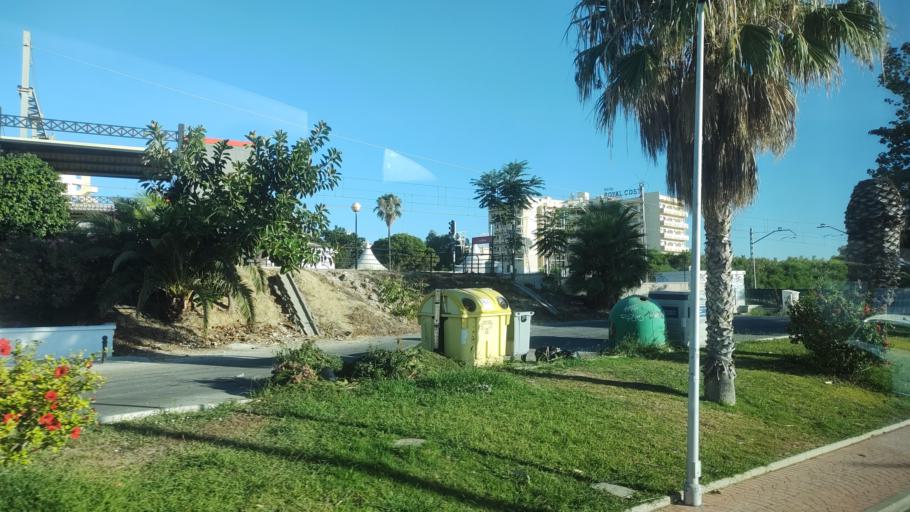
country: ES
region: Andalusia
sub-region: Provincia de Malaga
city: Torremolinos
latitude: 36.6450
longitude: -4.4848
